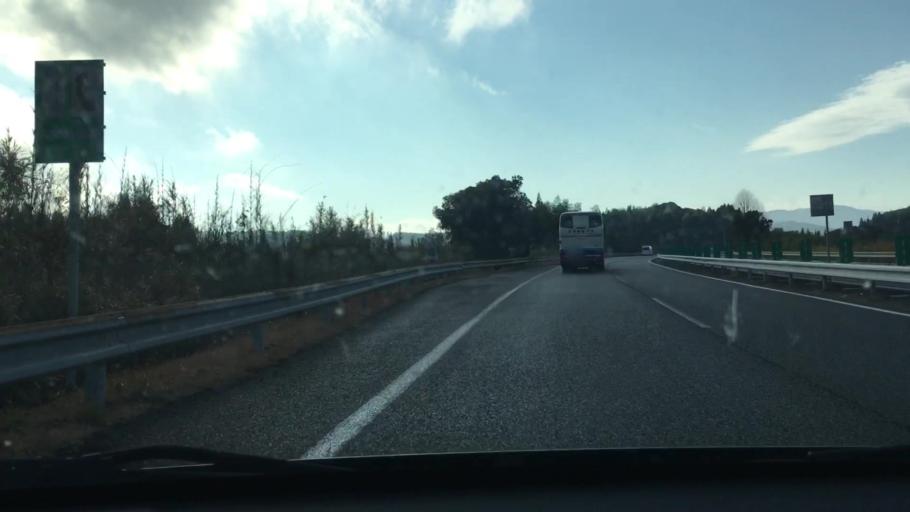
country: JP
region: Kagoshima
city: Okuchi-shinohara
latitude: 32.0247
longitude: 130.7912
